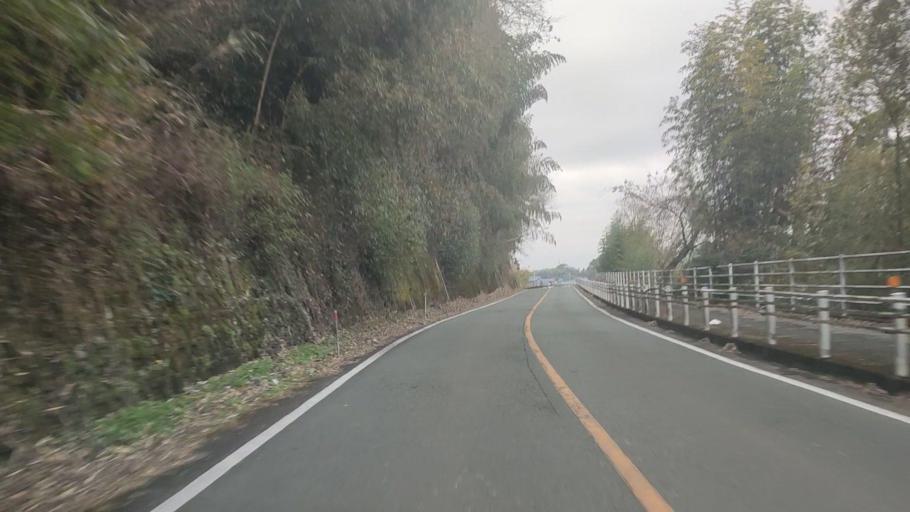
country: JP
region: Kumamoto
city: Ozu
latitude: 32.8523
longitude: 130.8669
